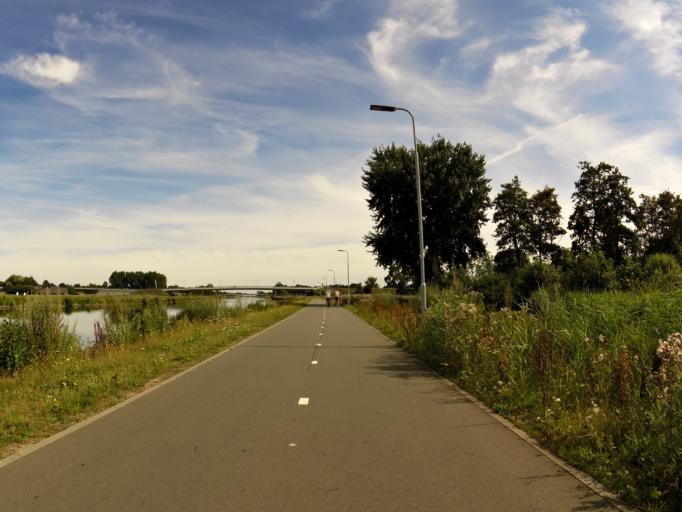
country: NL
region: North Brabant
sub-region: Gemeente 's-Hertogenbosch
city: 's-Hertogenbosch
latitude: 51.7217
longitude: 5.3408
